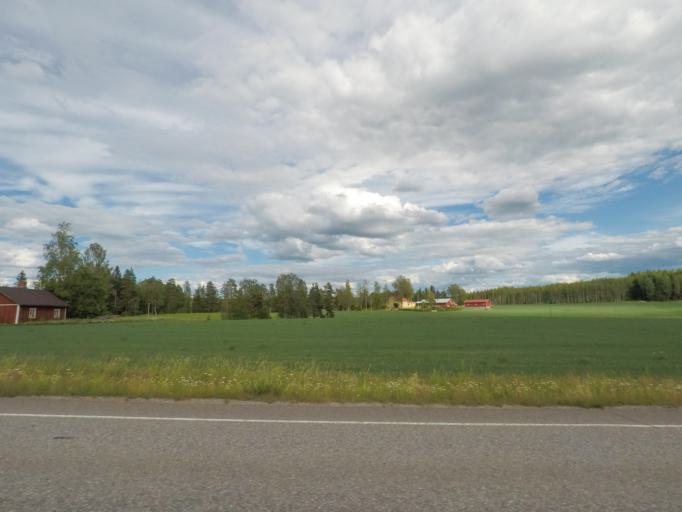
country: FI
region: Paijanne Tavastia
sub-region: Lahti
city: Hollola
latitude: 60.8493
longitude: 25.4958
